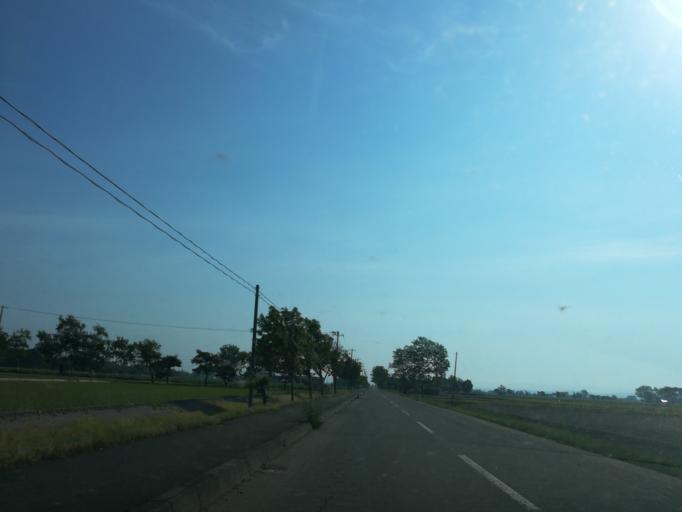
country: JP
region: Hokkaido
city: Iwamizawa
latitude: 43.1528
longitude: 141.6706
